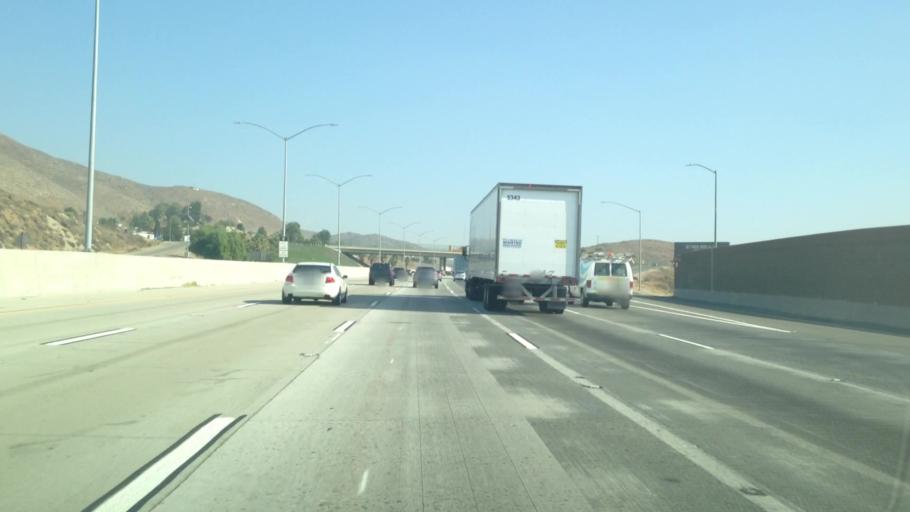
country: US
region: California
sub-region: Riverside County
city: Glen Avon
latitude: 34.0194
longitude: -117.4846
